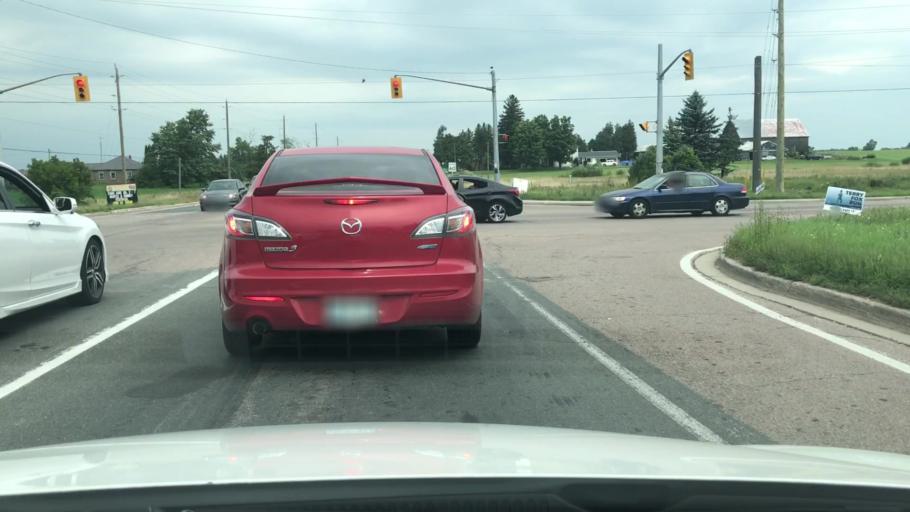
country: CA
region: Ontario
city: Innisfil
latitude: 44.2998
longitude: -79.6134
